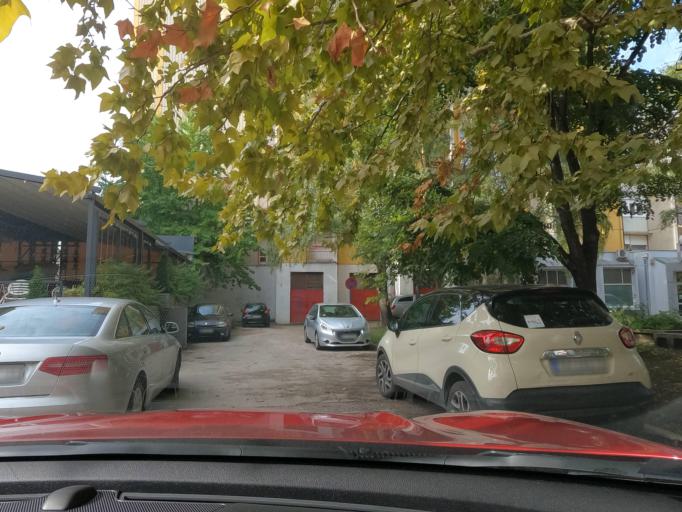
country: RS
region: Central Serbia
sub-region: Moravicki Okrug
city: Cacak
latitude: 43.8894
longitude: 20.3434
